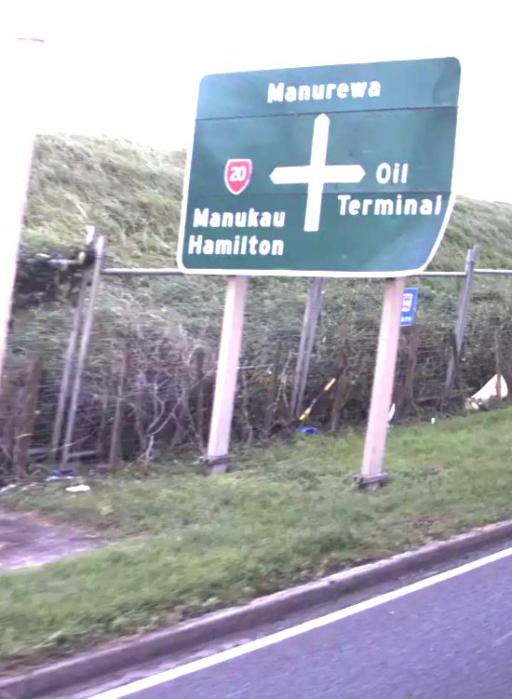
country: NZ
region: Auckland
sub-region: Auckland
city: Wiri
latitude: -37.0044
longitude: 174.8544
